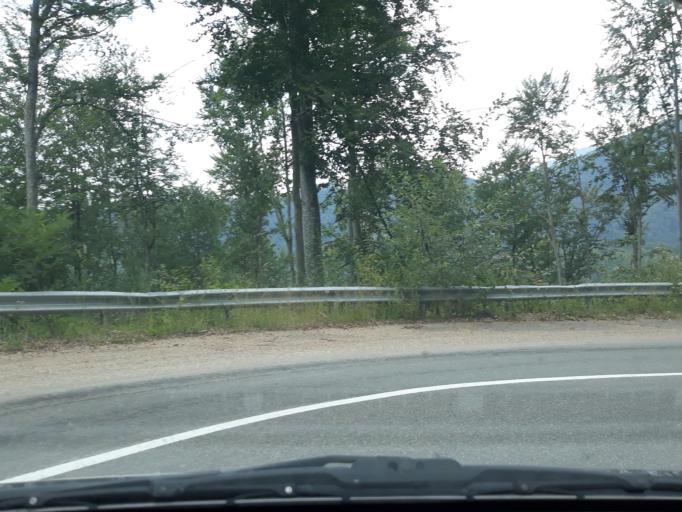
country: RO
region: Bihor
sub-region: Comuna Pietroasa
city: Pietroasa
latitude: 46.5967
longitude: 22.6558
